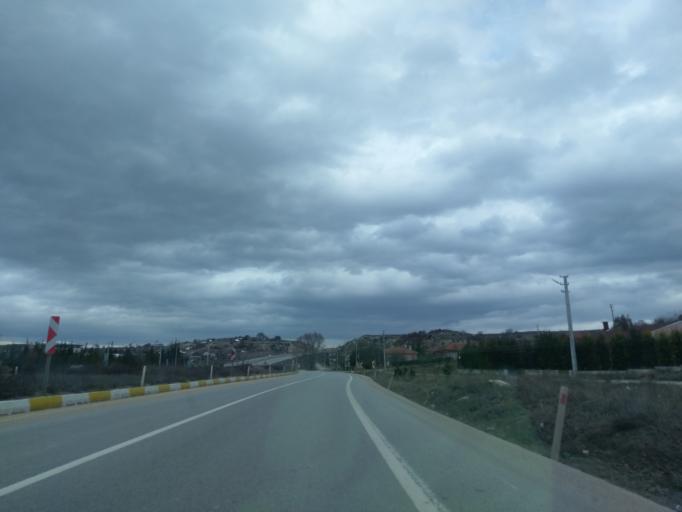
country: TR
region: Eskisehir
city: Eskisehir
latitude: 39.7331
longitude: 30.3821
